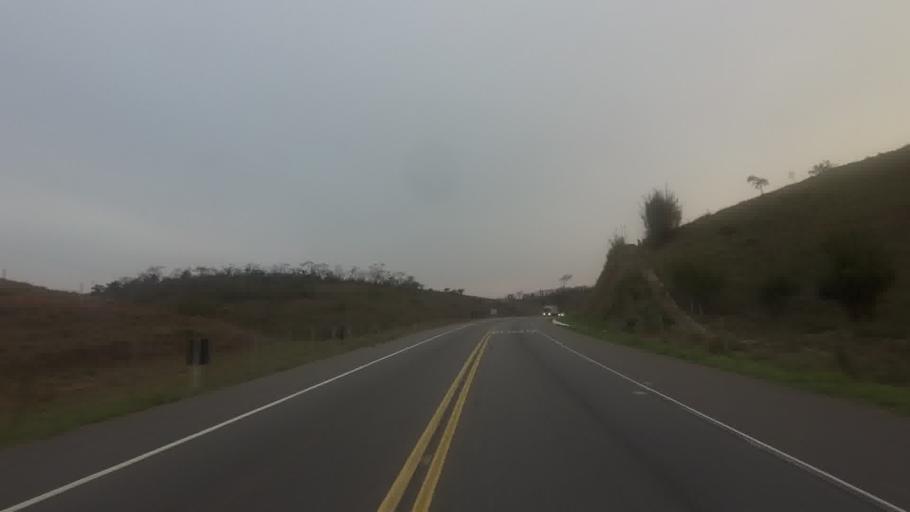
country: BR
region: Minas Gerais
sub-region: Recreio
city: Recreio
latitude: -21.7425
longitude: -42.4556
